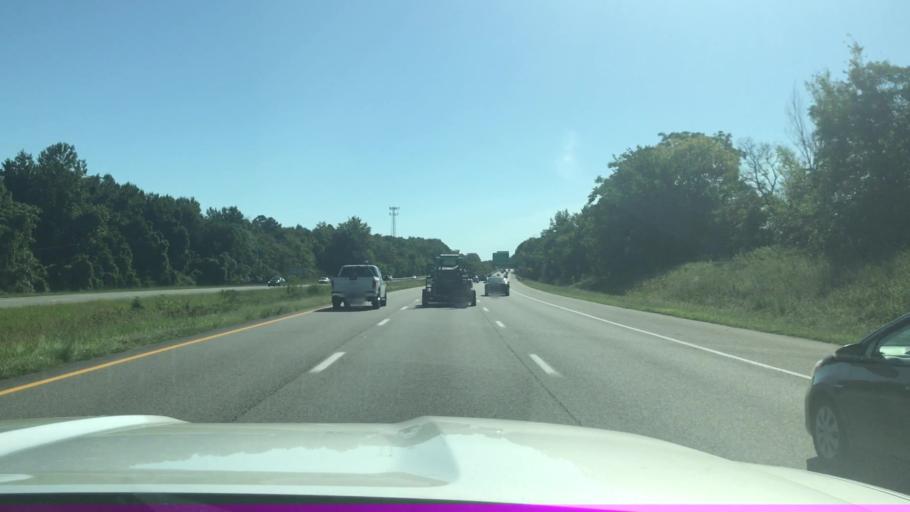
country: US
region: Virginia
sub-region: Henrico County
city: Montrose
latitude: 37.5324
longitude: -77.3539
